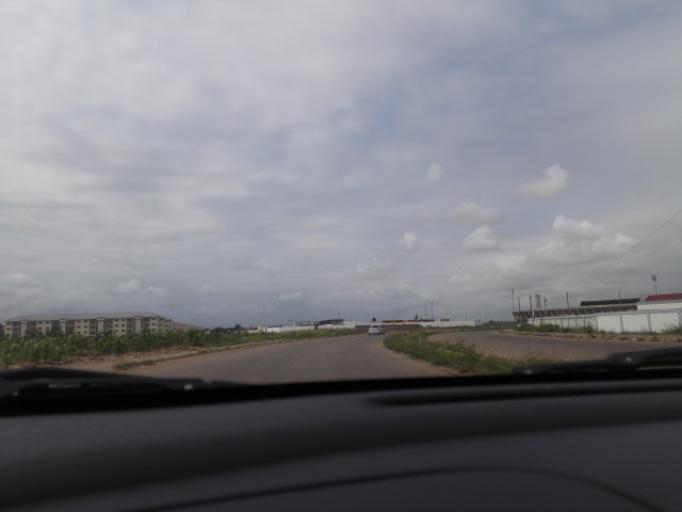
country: MZ
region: Maputo City
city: Maputo
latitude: -25.8229
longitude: 32.5824
